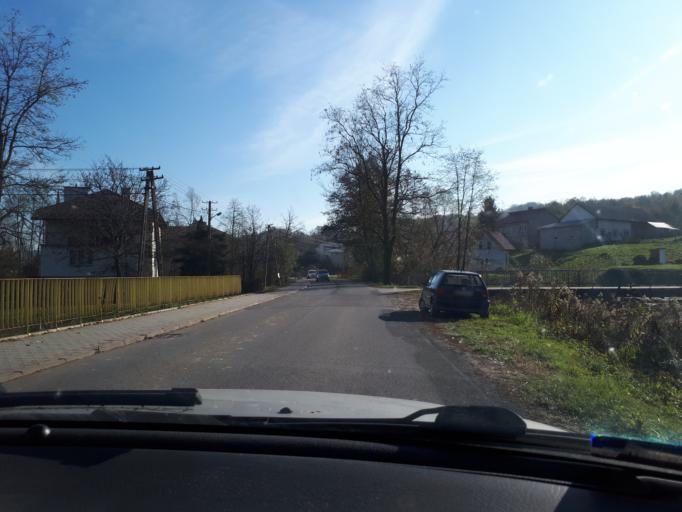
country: PL
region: Subcarpathian Voivodeship
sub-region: Powiat debicki
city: Debica
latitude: 49.9970
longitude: 21.4176
